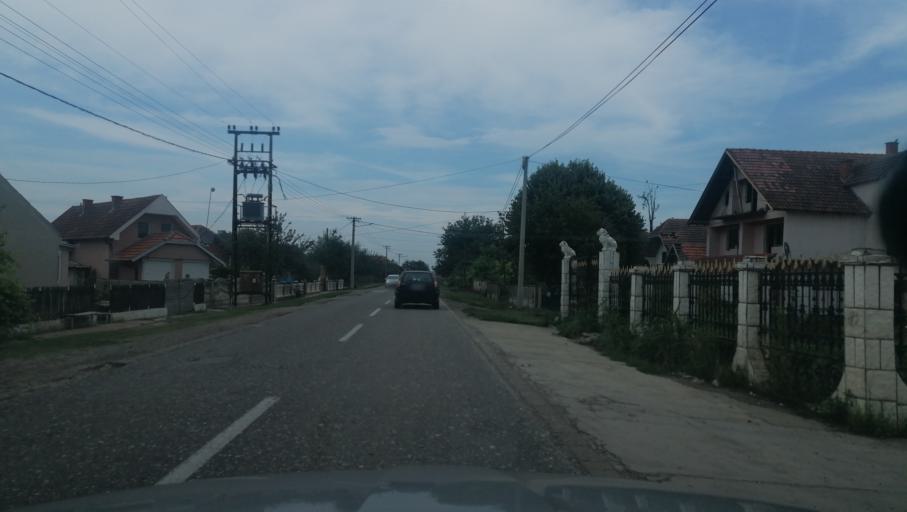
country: RS
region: Central Serbia
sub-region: Macvanski Okrug
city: Bogatic
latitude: 44.8299
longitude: 19.4661
